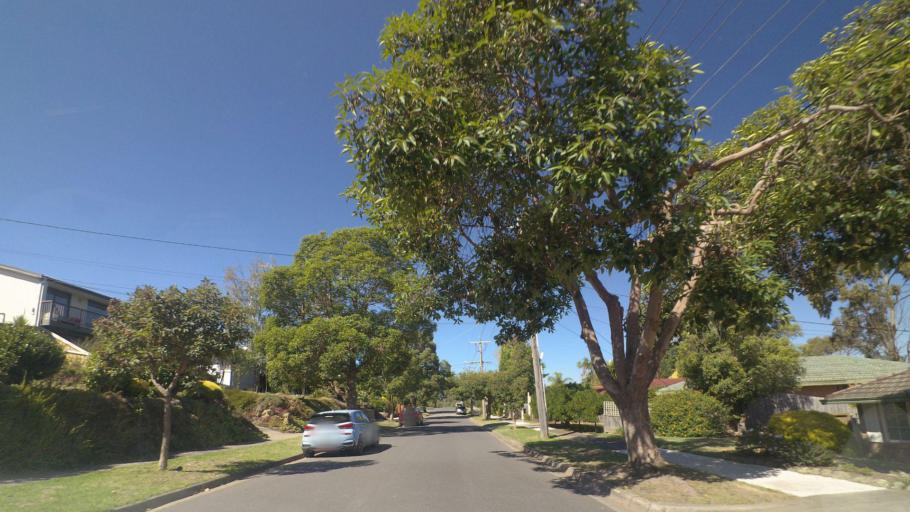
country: AU
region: Victoria
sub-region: Manningham
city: Donvale
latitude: -37.8020
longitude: 145.1725
